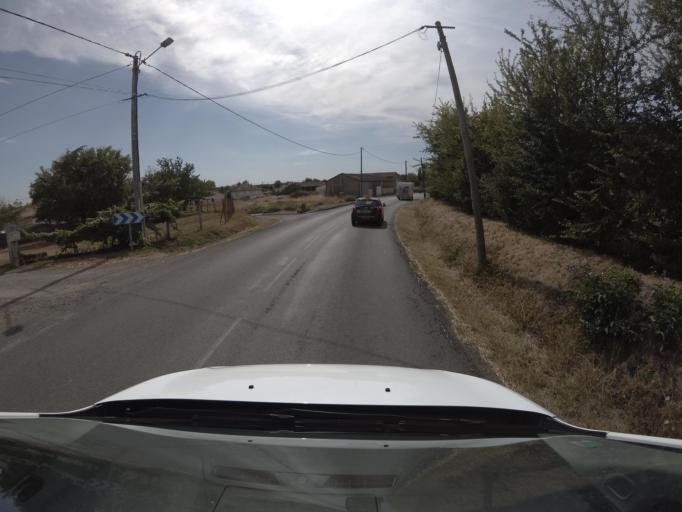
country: FR
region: Poitou-Charentes
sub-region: Departement des Deux-Sevres
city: Saint-Leger-de-Montbrun
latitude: 46.9954
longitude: -0.1179
